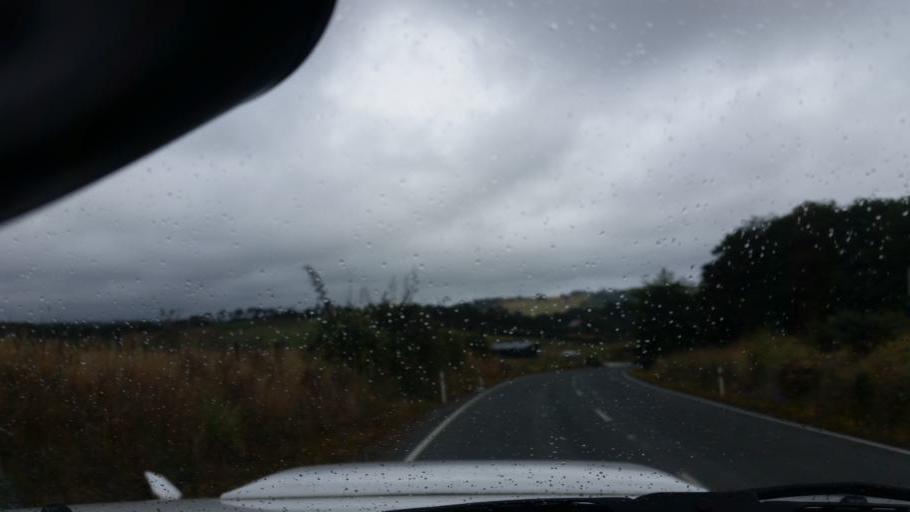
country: NZ
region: Auckland
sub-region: Auckland
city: Wellsford
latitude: -36.1420
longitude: 174.5000
